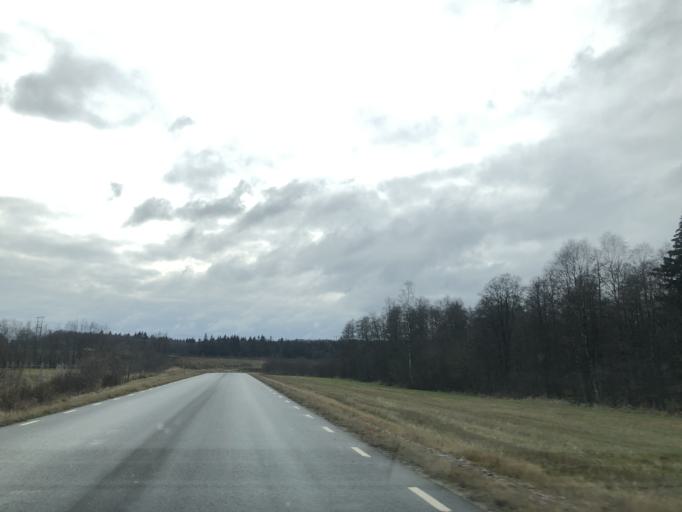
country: SE
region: Vaestra Goetaland
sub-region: Ulricehamns Kommun
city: Ulricehamn
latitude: 57.8118
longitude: 13.2411
